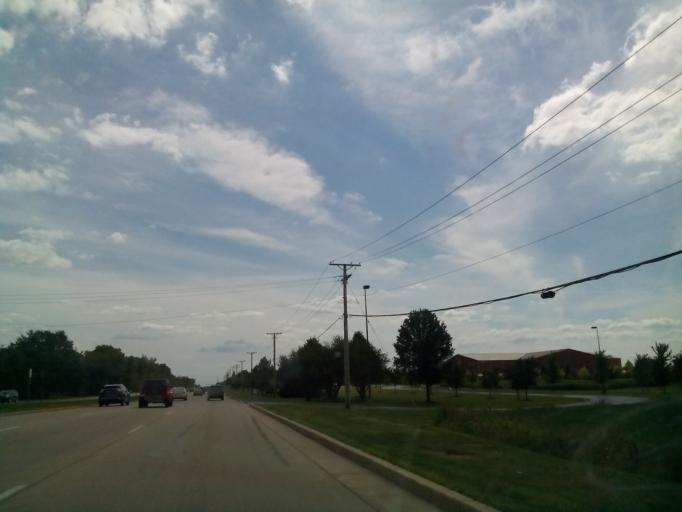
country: US
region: Illinois
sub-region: DuPage County
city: Naperville
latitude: 41.7403
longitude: -88.2062
